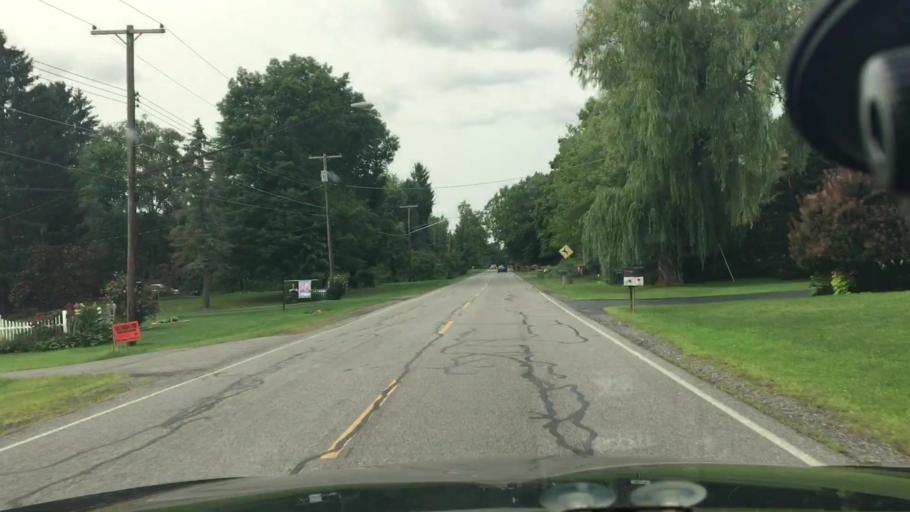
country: US
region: New York
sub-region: Erie County
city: Orchard Park
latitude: 42.7157
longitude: -78.7314
